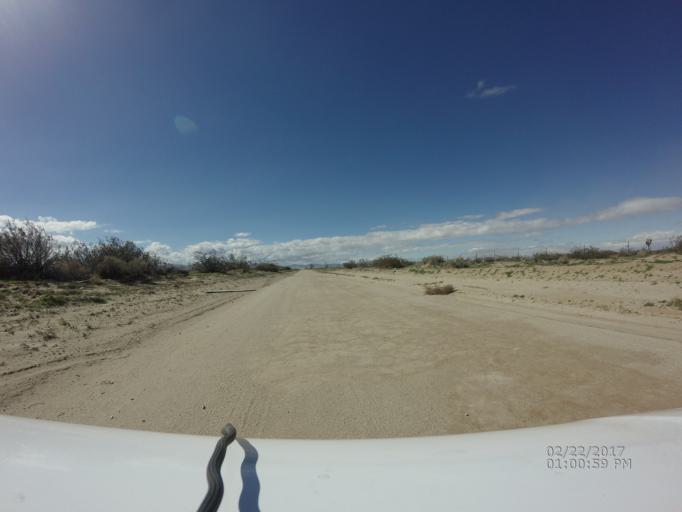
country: US
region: California
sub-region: Los Angeles County
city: Littlerock
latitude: 34.6019
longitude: -117.9589
